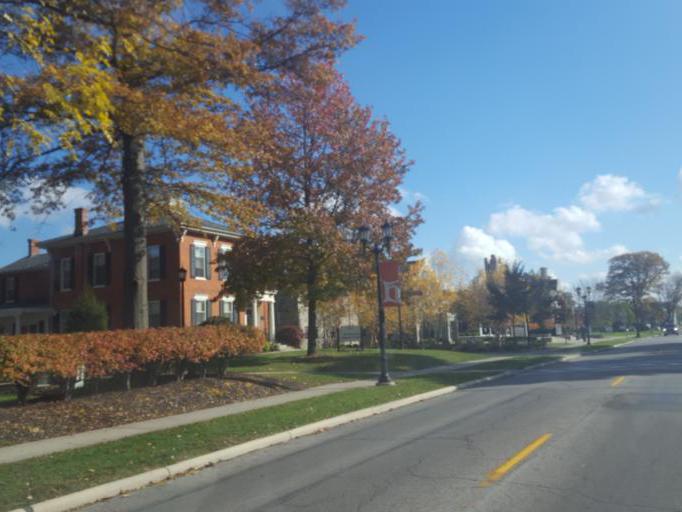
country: US
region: Ohio
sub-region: Seneca County
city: Tiffin
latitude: 41.1157
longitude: -83.1676
